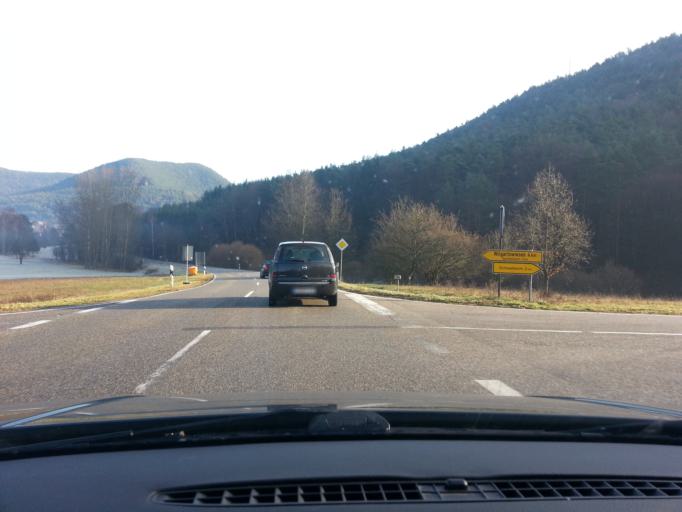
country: DE
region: Rheinland-Pfalz
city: Schwanheim
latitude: 49.1809
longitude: 7.8840
